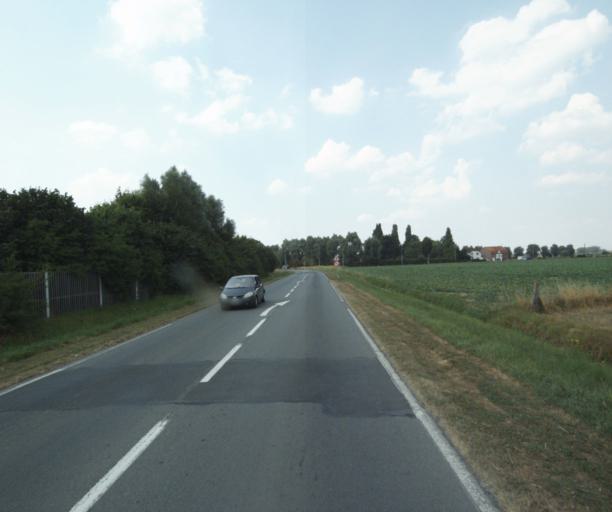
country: FR
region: Nord-Pas-de-Calais
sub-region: Departement du Nord
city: Comines
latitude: 50.7406
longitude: 3.0161
